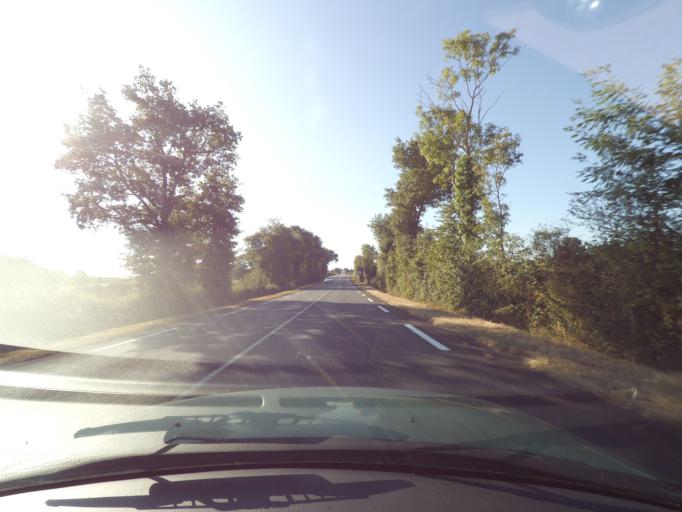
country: FR
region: Poitou-Charentes
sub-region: Departement des Deux-Sevres
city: Chiche
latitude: 46.7760
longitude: -0.3265
